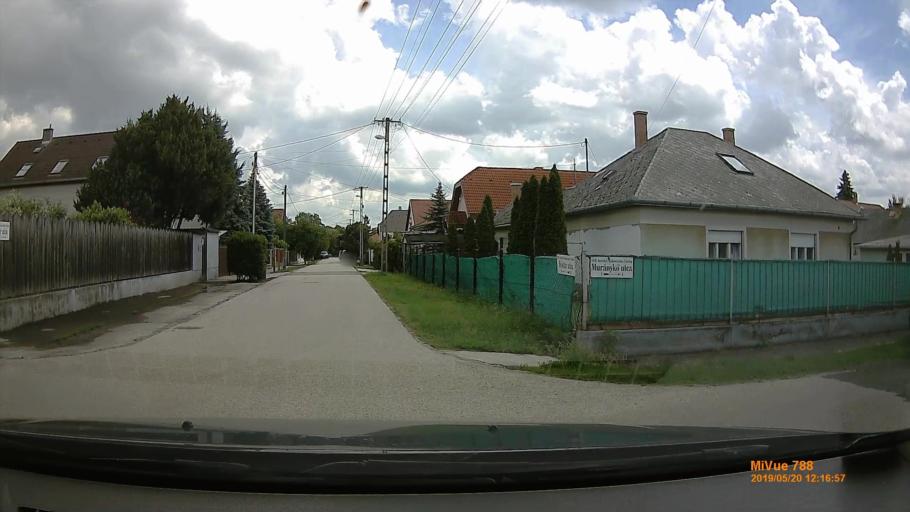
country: HU
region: Budapest
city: Budapest XVII. keruelet
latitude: 47.4990
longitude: 19.2746
